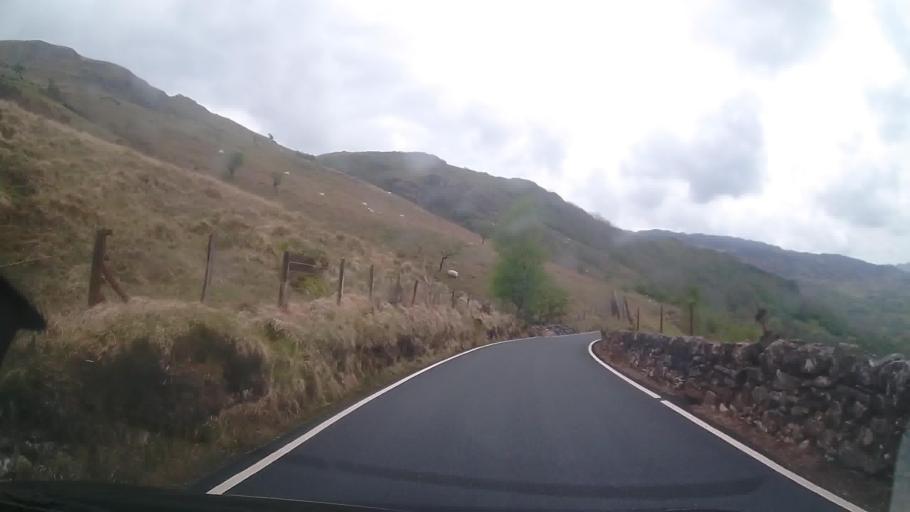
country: GB
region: Wales
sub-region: Gwynedd
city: Blaenau-Ffestiniog
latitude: 53.0663
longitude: -4.0022
